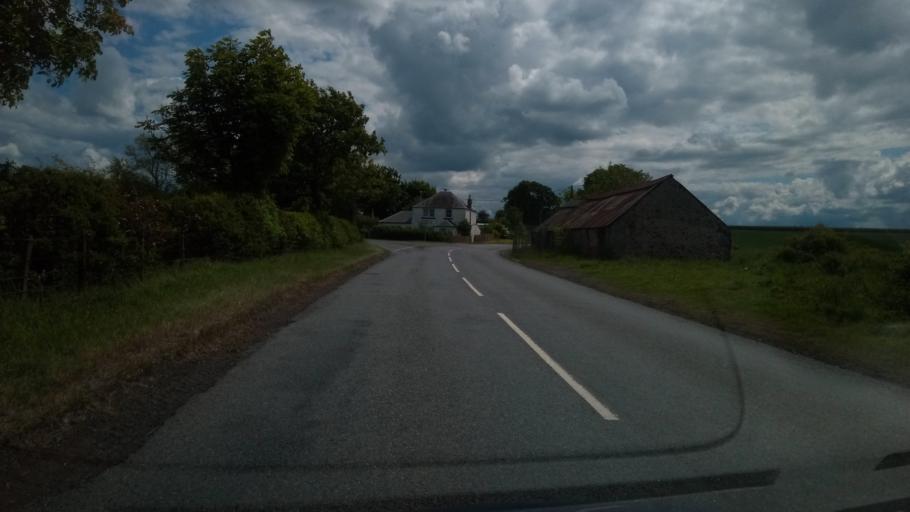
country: GB
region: Scotland
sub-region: The Scottish Borders
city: Kelso
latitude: 55.5792
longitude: -2.4066
